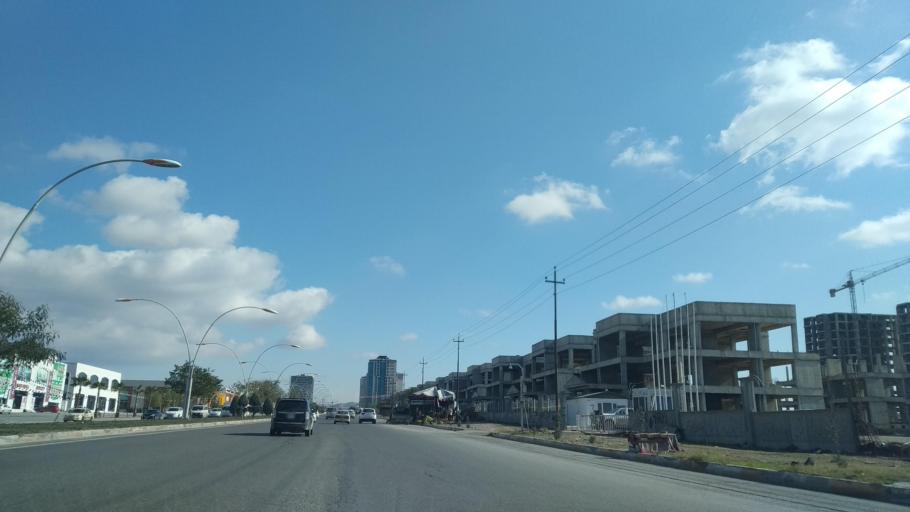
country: IQ
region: Arbil
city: Erbil
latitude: 36.2032
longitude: 44.1093
